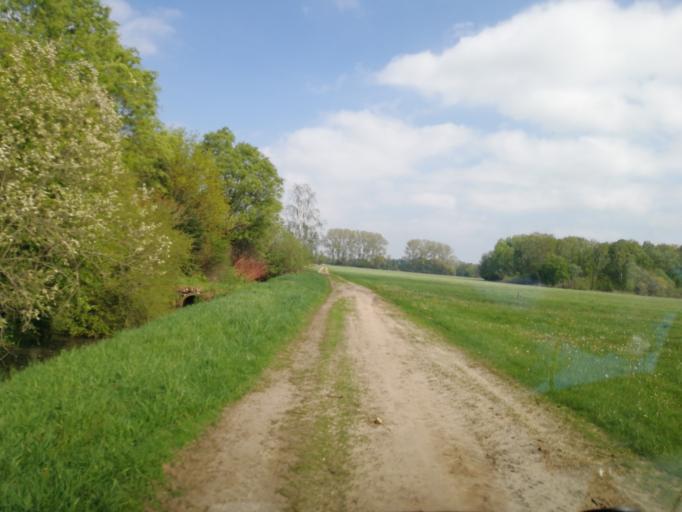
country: DE
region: Brandenburg
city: Doberlug-Kirchhain
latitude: 51.6753
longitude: 13.5519
